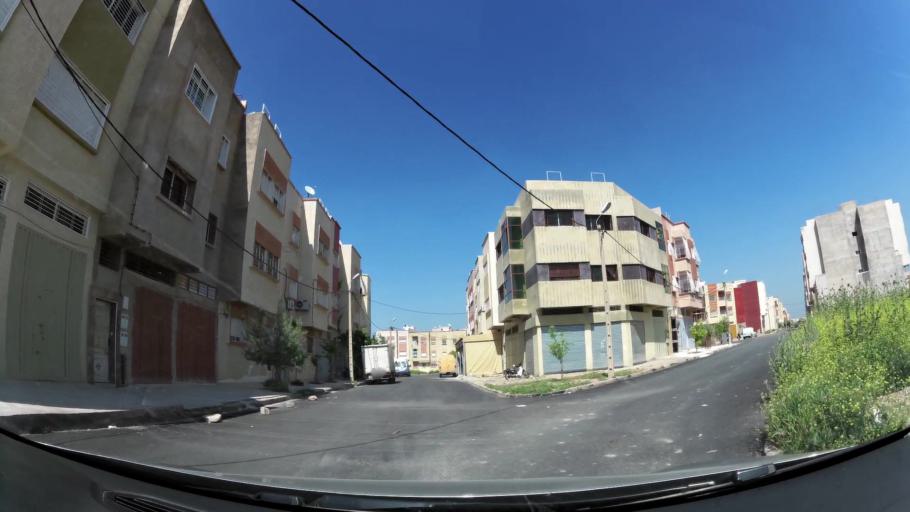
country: MA
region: Fes-Boulemane
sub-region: Fes
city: Fes
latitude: 34.0079
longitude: -5.0352
